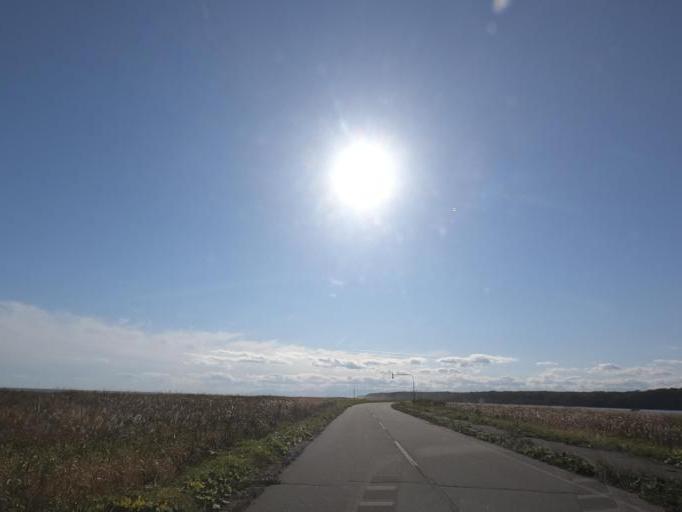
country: JP
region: Hokkaido
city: Obihiro
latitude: 42.5886
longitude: 143.5382
